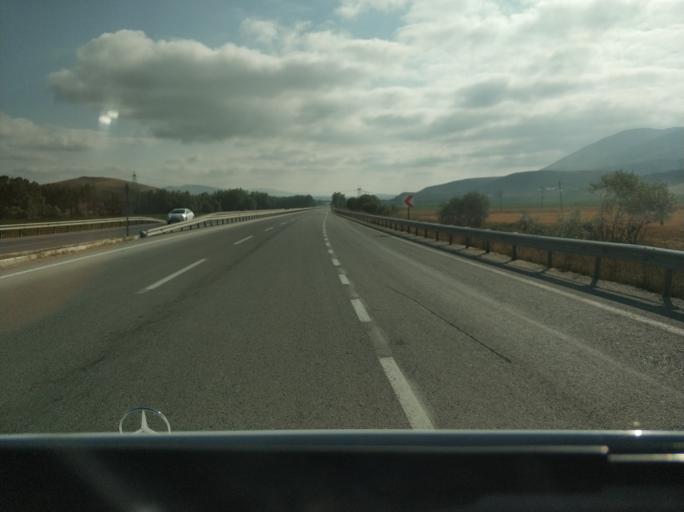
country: TR
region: Sivas
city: Yildizeli
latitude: 39.8499
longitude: 36.5297
